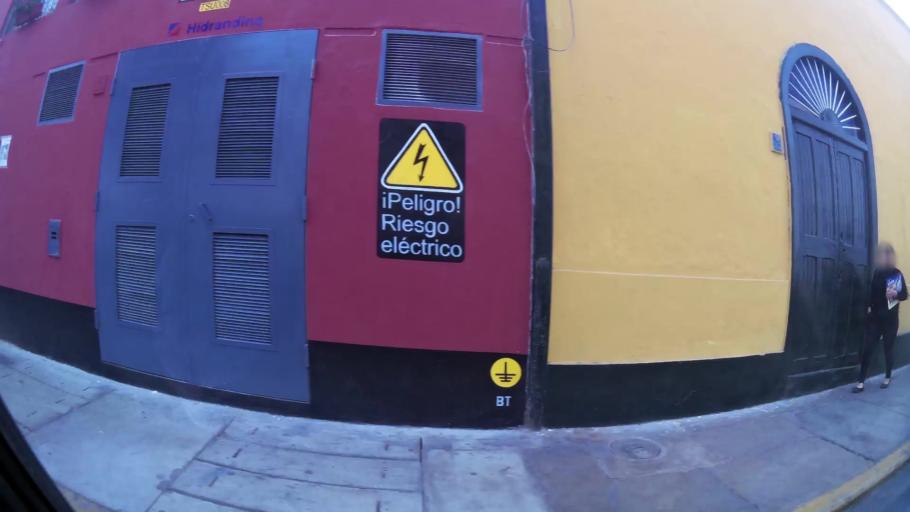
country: PE
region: La Libertad
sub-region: Provincia de Trujillo
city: Trujillo
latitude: -8.1083
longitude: -79.0265
